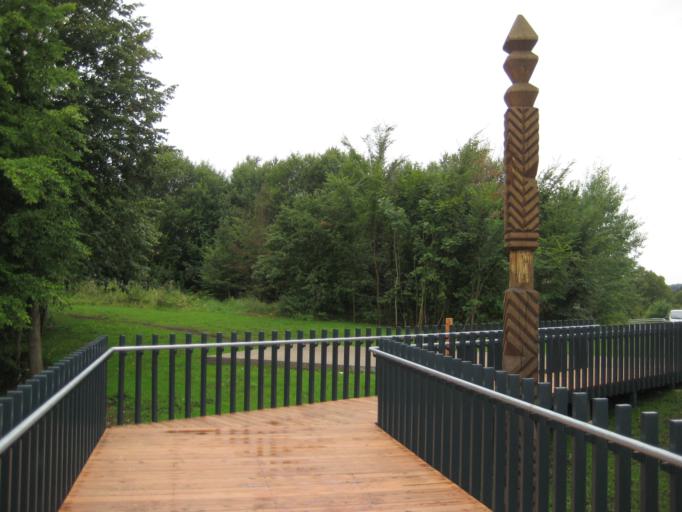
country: LT
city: Prienai
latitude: 54.5341
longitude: 23.8840
